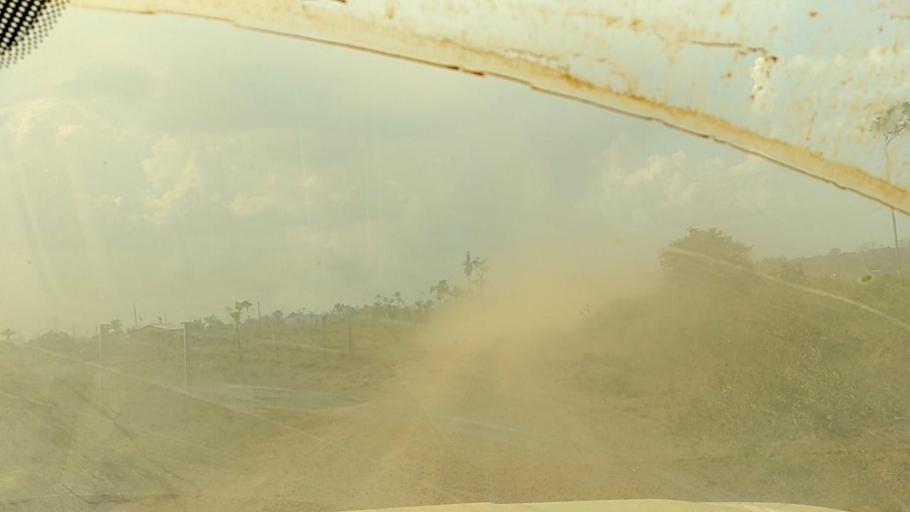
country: BR
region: Rondonia
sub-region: Porto Velho
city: Porto Velho
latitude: -8.6860
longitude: -63.2392
